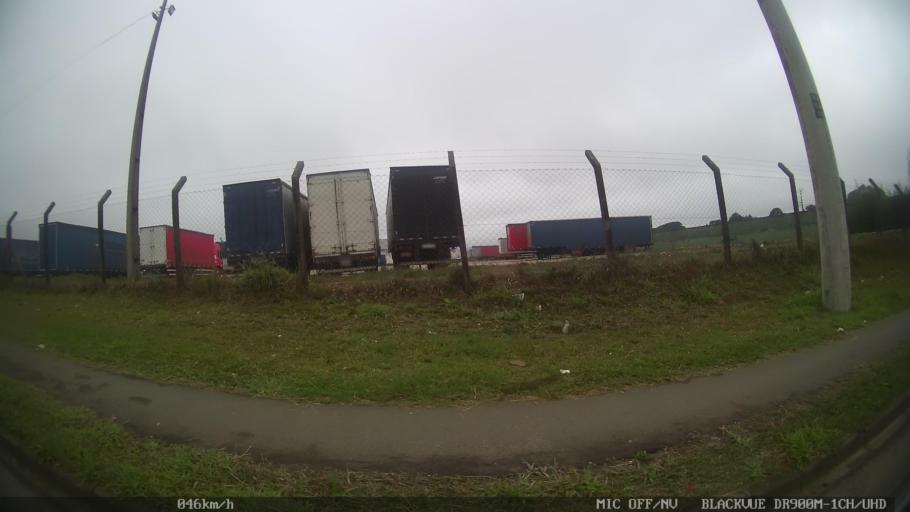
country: BR
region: Parana
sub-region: Sao Jose Dos Pinhais
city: Sao Jose dos Pinhais
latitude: -25.5696
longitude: -49.1726
